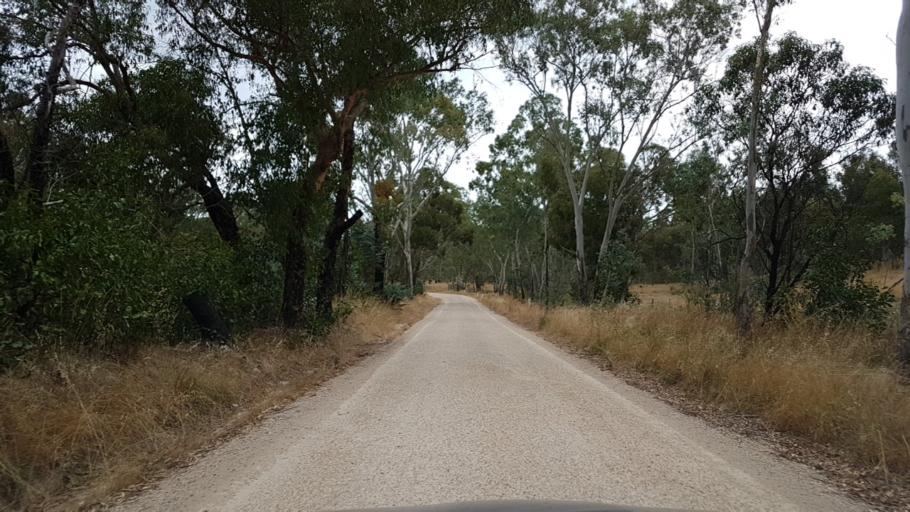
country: AU
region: South Australia
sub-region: Adelaide Hills
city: Gumeracha
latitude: -34.8053
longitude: 138.8338
